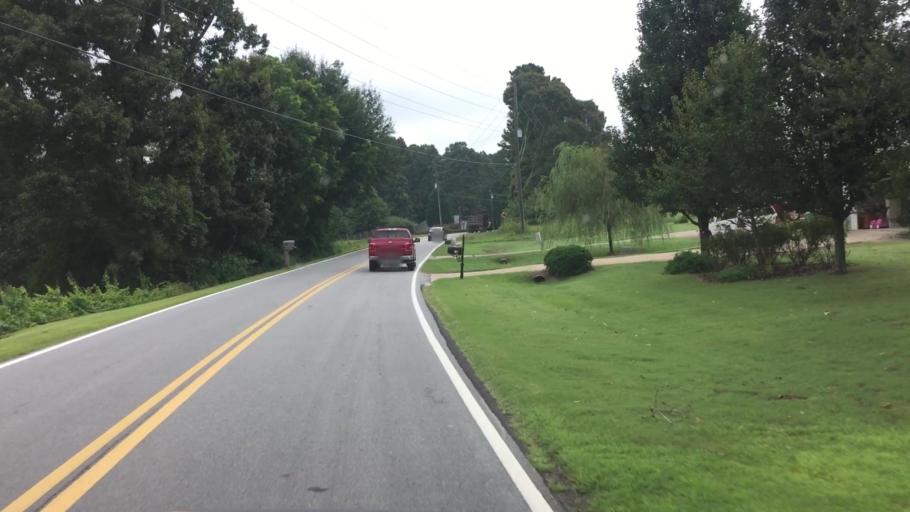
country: US
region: Georgia
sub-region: Barrow County
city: Winder
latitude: 34.0304
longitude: -83.7311
